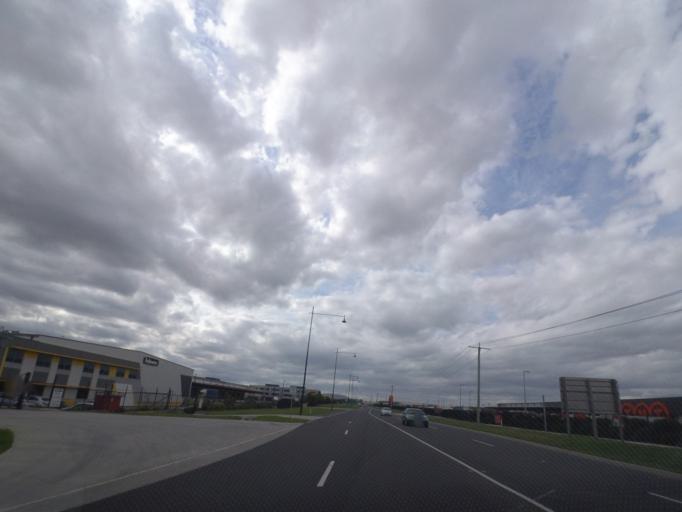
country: AU
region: Victoria
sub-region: Brimbank
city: Keilor Park
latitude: -37.6969
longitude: 144.8566
